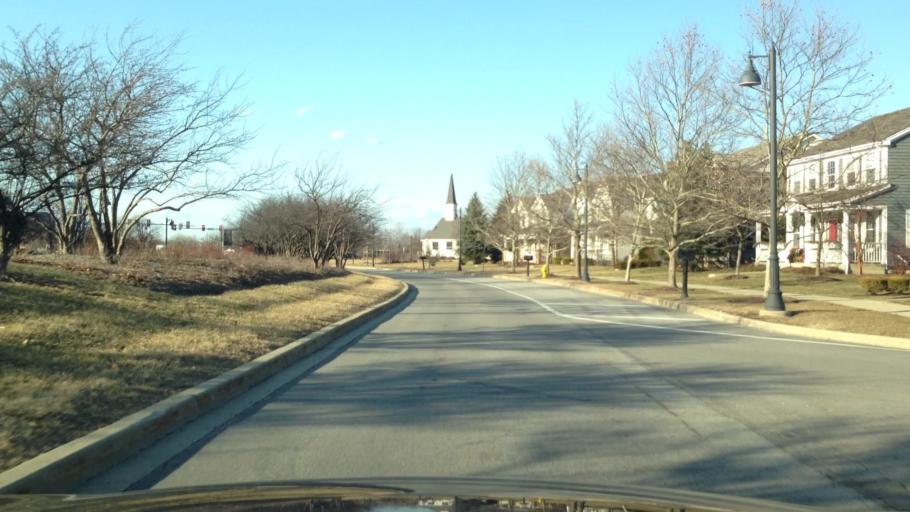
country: US
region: Illinois
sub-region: Cook County
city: Glenview
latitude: 42.0853
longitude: -87.8211
